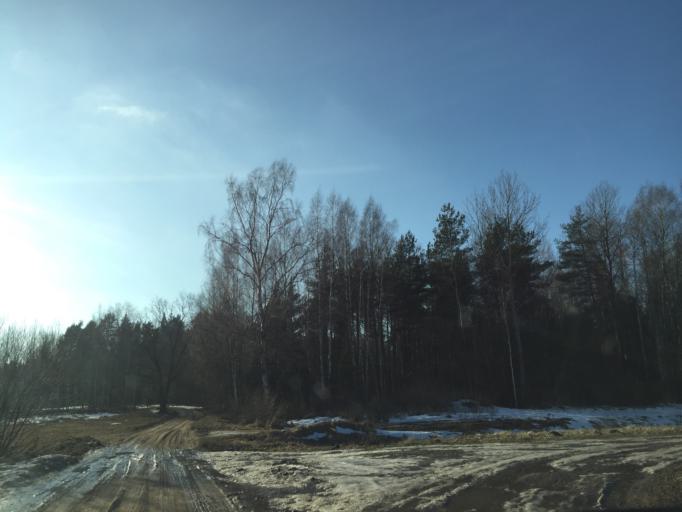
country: LV
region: Lecava
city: Iecava
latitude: 56.6794
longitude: 24.2003
